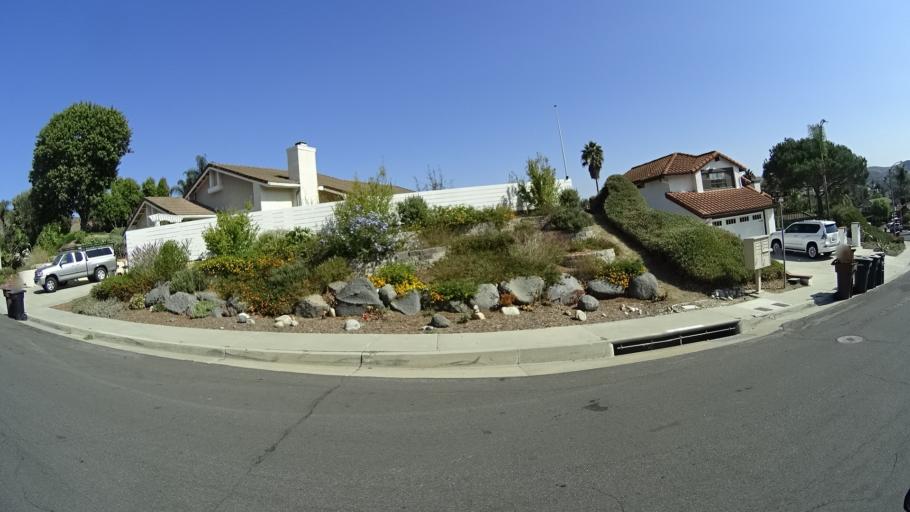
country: US
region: California
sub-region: Orange County
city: San Juan Capistrano
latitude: 33.4709
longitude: -117.6387
